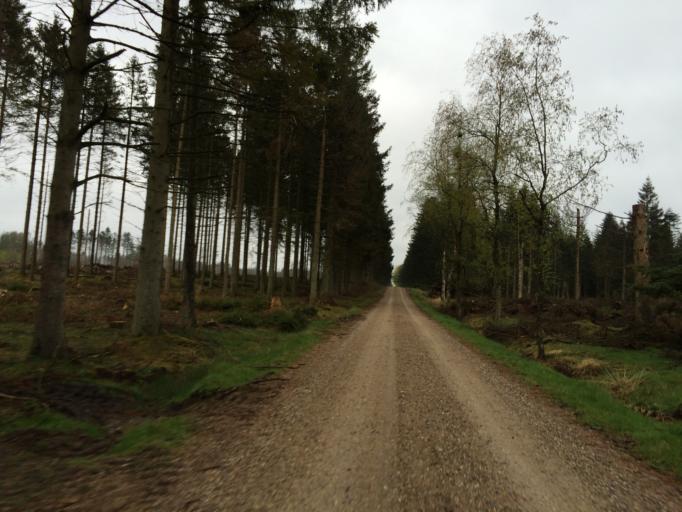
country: DK
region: Central Jutland
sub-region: Holstebro Kommune
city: Ulfborg
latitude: 56.2609
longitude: 8.4423
